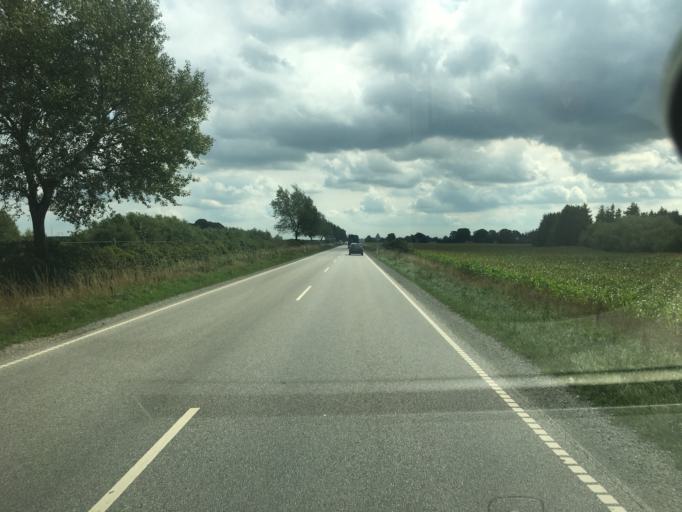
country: DK
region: South Denmark
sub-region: Aabenraa Kommune
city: Tinglev
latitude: 54.9740
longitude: 9.3053
